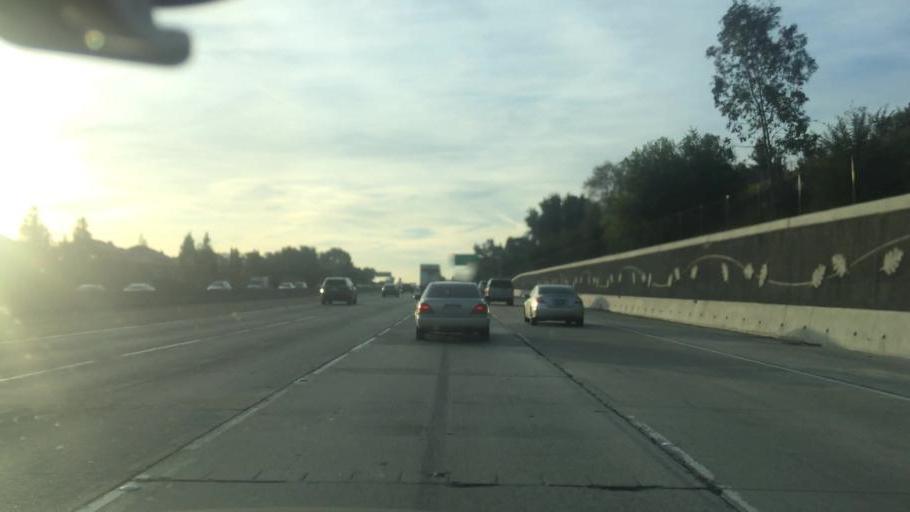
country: US
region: California
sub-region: Contra Costa County
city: San Ramon
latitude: 37.7921
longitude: -121.9831
